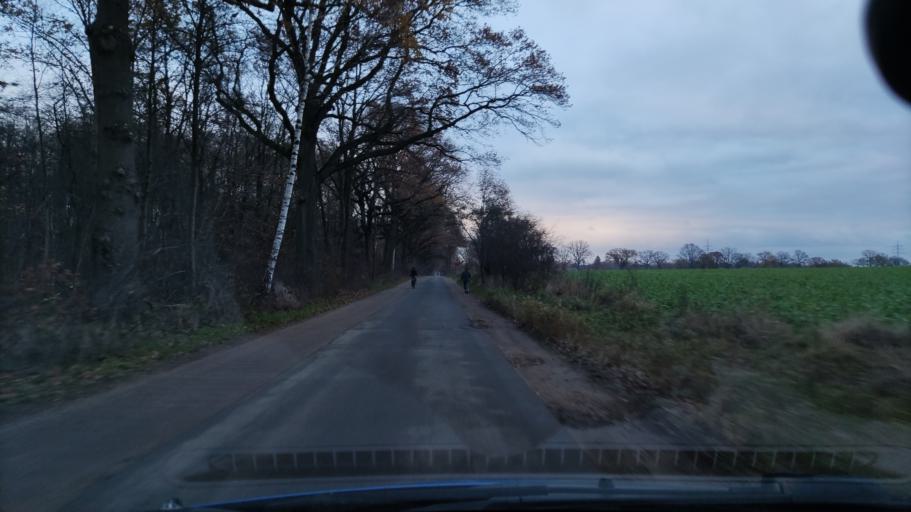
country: DE
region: Lower Saxony
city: Reppenstedt
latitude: 53.2591
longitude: 10.3652
